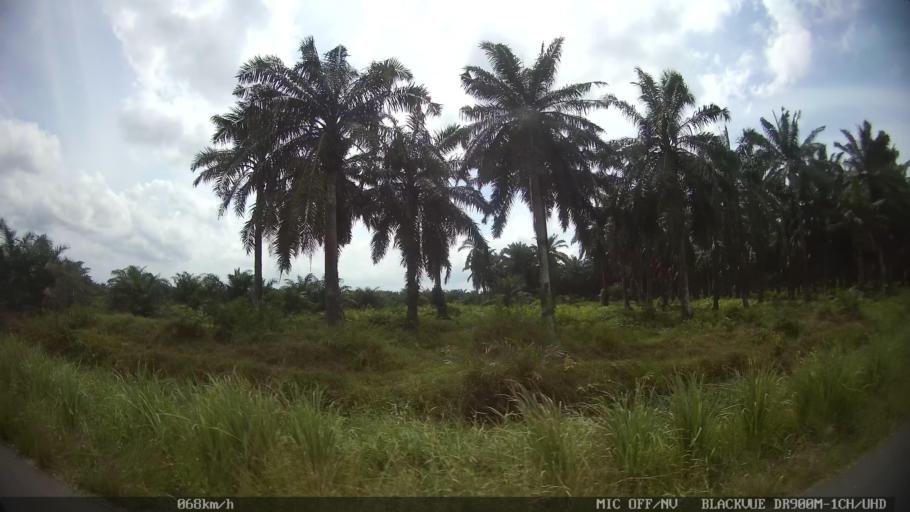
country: ID
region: North Sumatra
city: Percut
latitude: 3.5901
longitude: 98.8408
